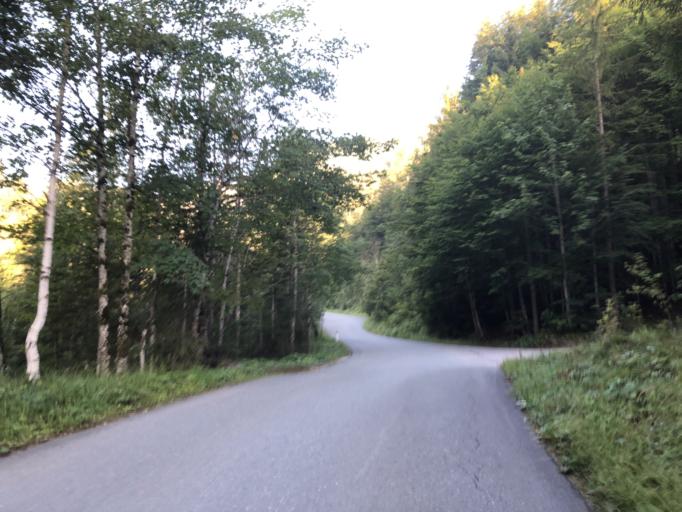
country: AT
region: Tyrol
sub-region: Politischer Bezirk Kitzbuhel
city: Schwendt
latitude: 47.5821
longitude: 12.3582
